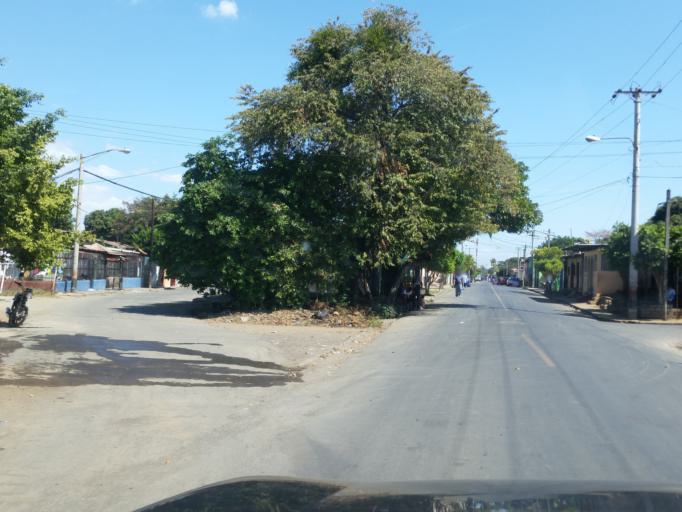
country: NI
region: Managua
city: Managua
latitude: 12.1597
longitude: -86.2864
